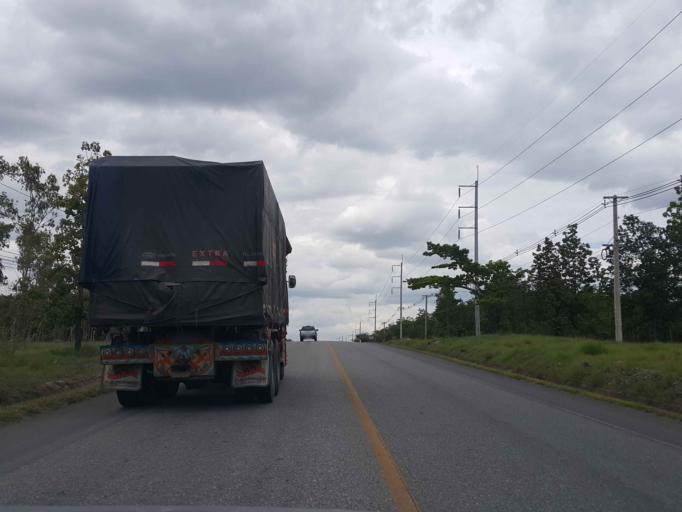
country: TH
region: Lamphun
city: Ban Hong
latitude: 18.4036
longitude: 98.8392
